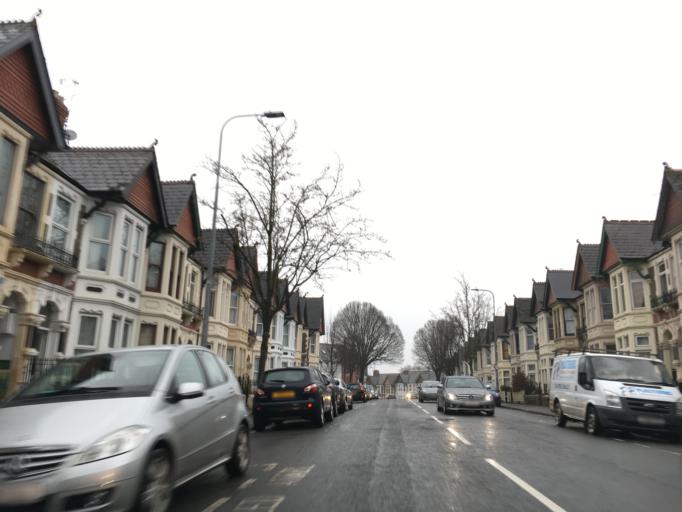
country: GB
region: Wales
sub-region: Cardiff
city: Cardiff
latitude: 51.5006
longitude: -3.1756
